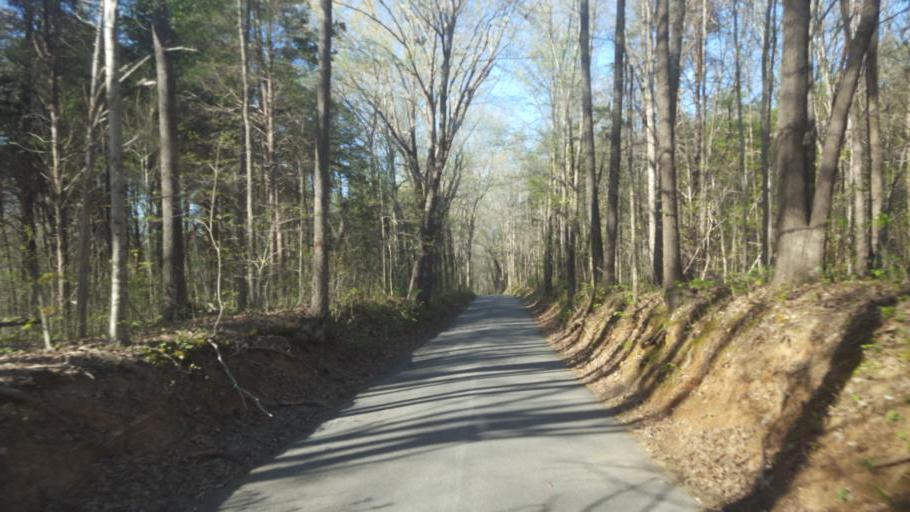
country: US
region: Kentucky
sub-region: Barren County
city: Cave City
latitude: 37.1838
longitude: -86.0489
